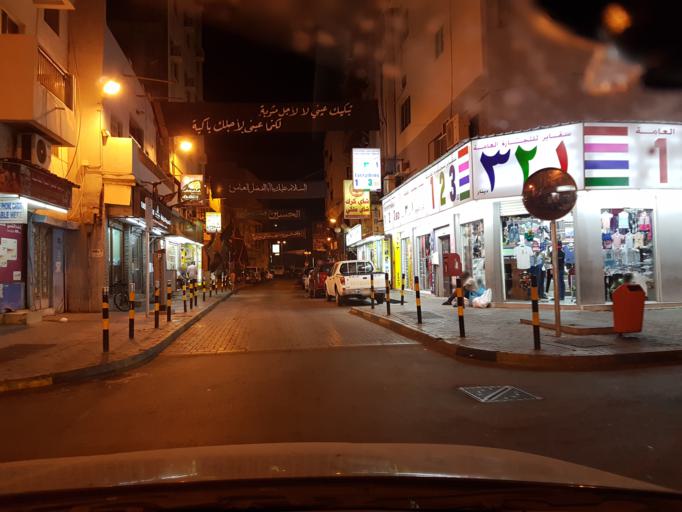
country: BH
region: Manama
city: Manama
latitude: 26.2322
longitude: 50.5806
